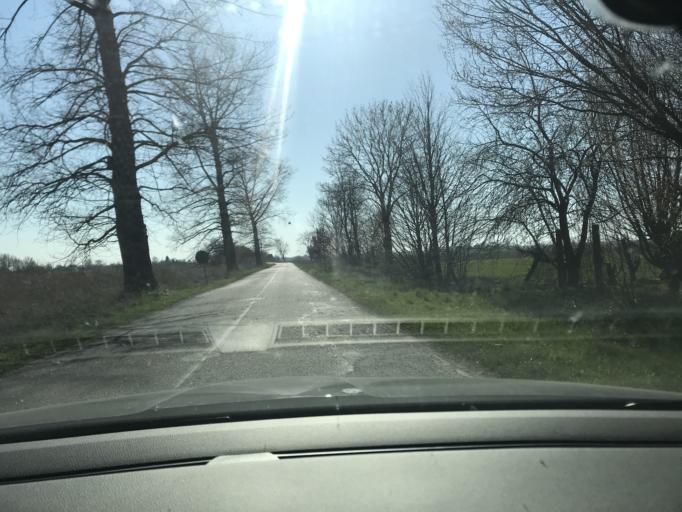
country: PL
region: Pomeranian Voivodeship
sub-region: Powiat nowodworski
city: Sztutowo
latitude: 54.3107
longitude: 19.1588
